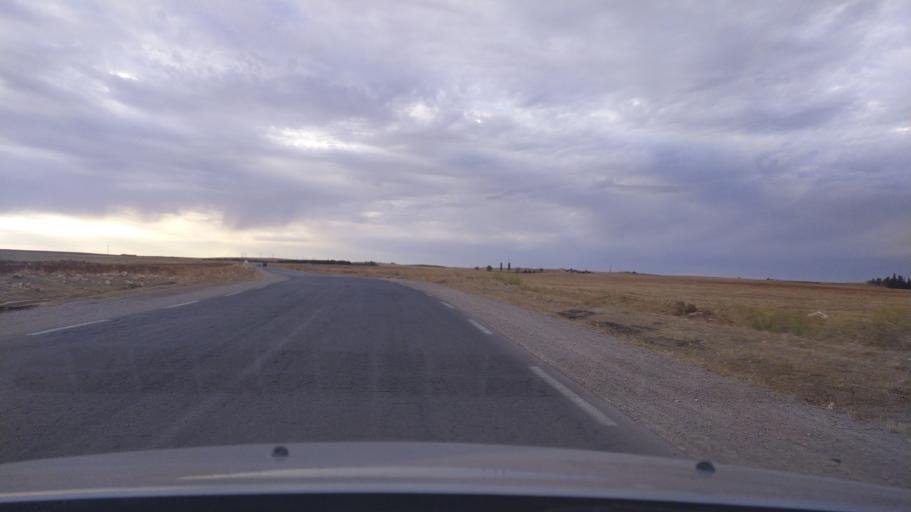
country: DZ
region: Tiaret
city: Frenda
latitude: 34.9801
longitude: 1.1510
